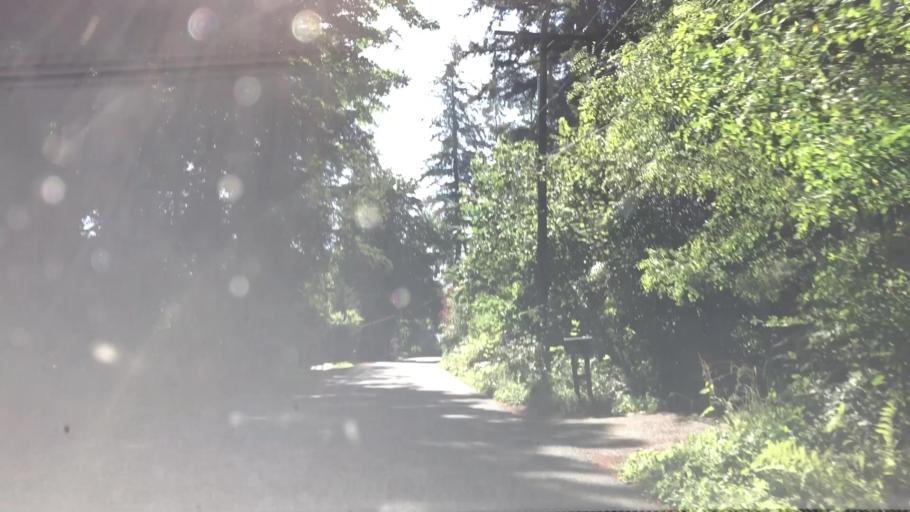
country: US
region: Washington
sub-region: King County
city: Cottage Lake
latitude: 47.7600
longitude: -122.0888
